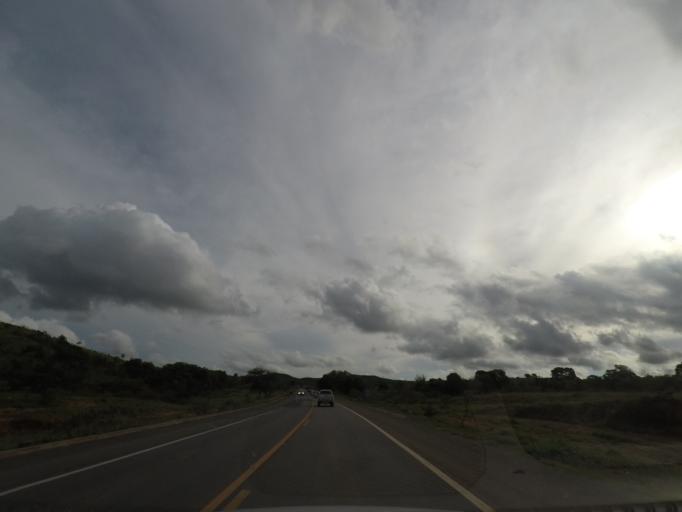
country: BR
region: Goias
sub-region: Pirenopolis
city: Pirenopolis
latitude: -15.7394
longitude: -48.7223
